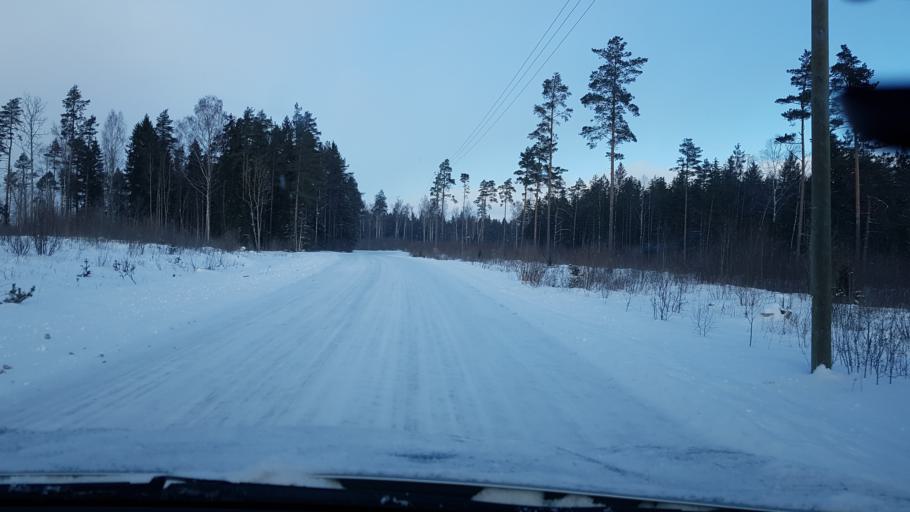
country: EE
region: Harju
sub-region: Nissi vald
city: Turba
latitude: 59.1921
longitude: 24.1399
